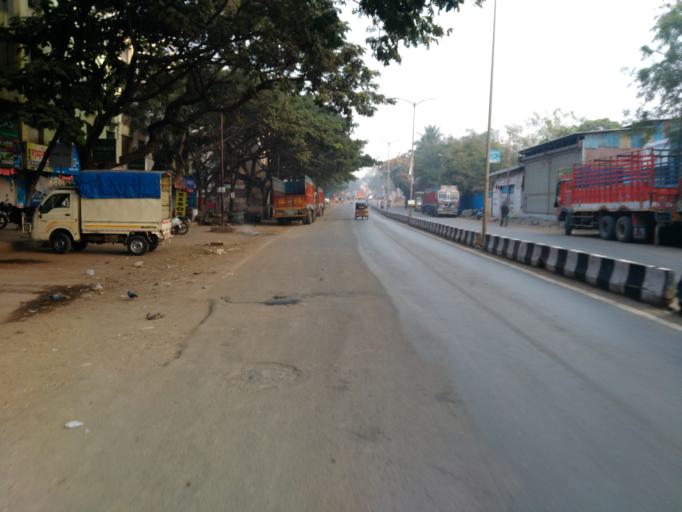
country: IN
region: Maharashtra
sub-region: Pune Division
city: Pune
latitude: 18.4551
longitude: 73.8907
